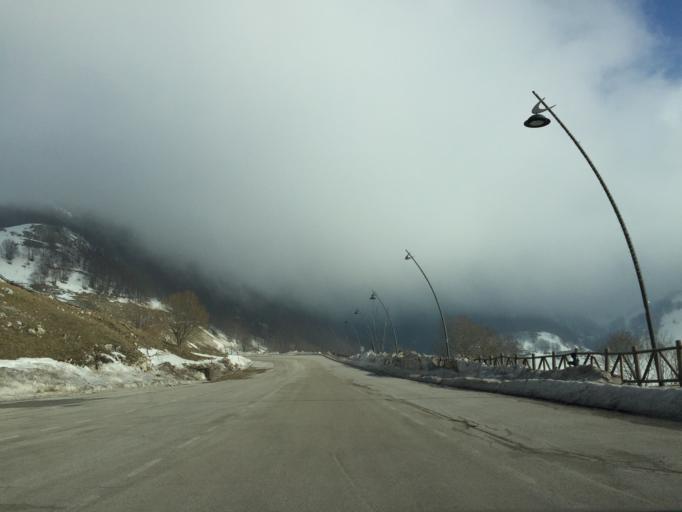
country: IT
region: Molise
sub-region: Provincia di Campobasso
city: San Massimo
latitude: 41.4616
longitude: 14.3930
